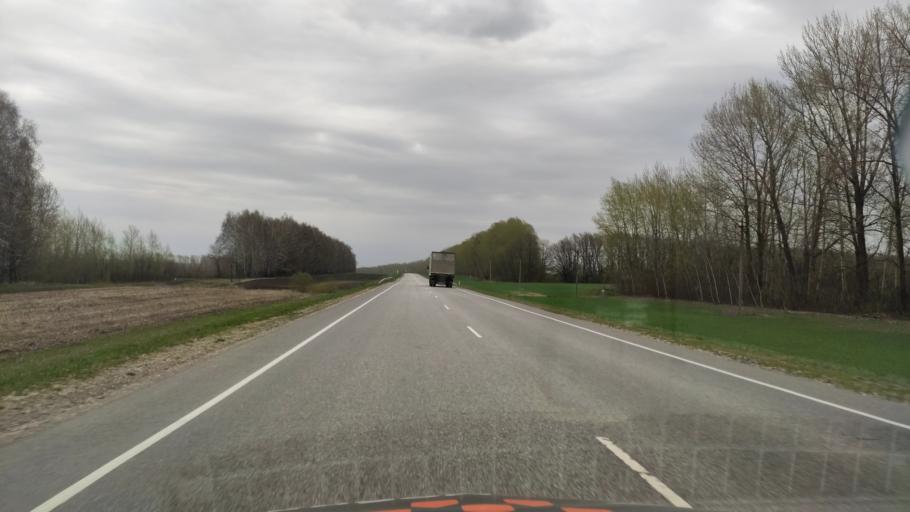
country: RU
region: Kursk
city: Olym
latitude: 51.5502
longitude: 38.1887
